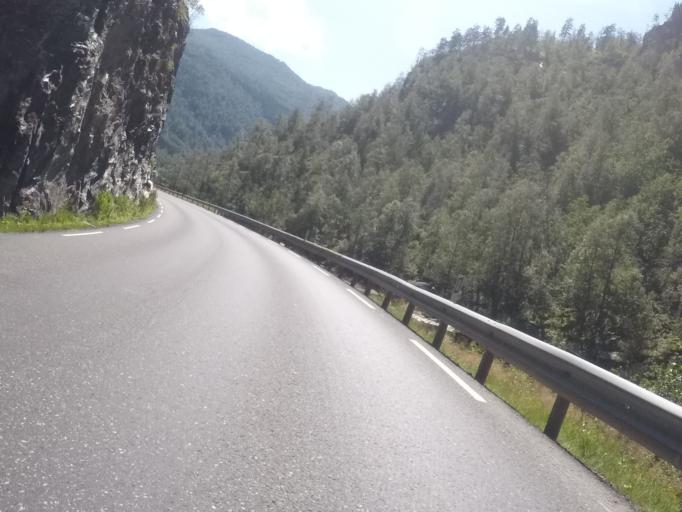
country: NO
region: Hordaland
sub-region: Voss
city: Voss
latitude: 60.7595
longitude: 6.4909
